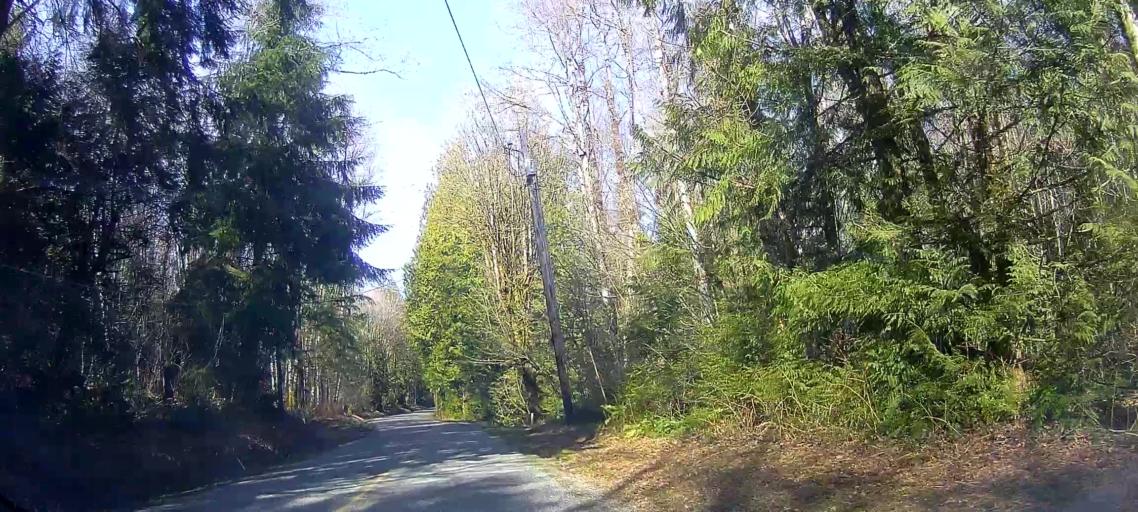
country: US
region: Washington
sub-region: Whatcom County
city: Sudden Valley
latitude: 48.6129
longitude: -122.3670
